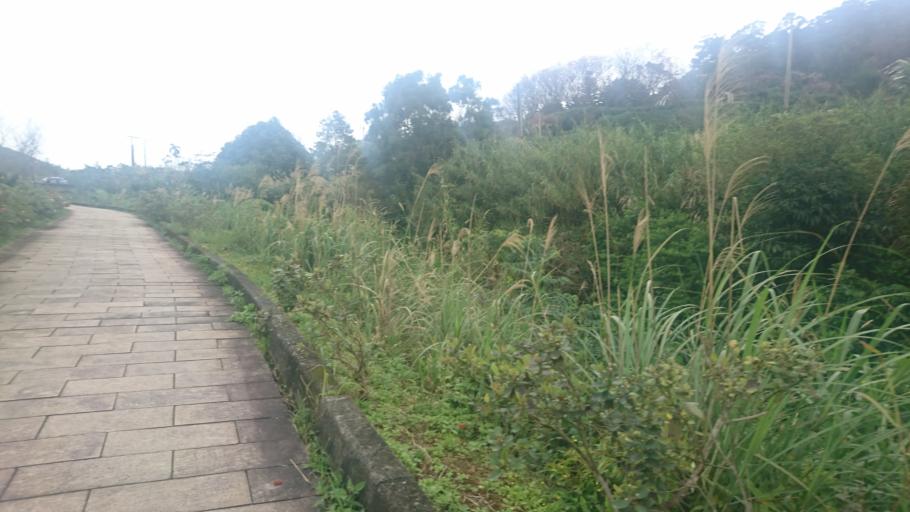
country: TW
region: Taipei
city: Taipei
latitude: 25.2641
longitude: 121.5159
